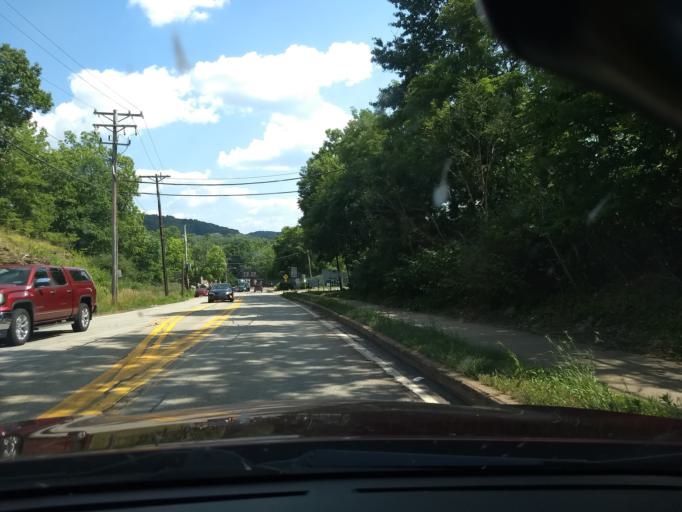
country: US
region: Pennsylvania
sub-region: Westmoreland County
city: Trafford
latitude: 40.3882
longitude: -79.7655
